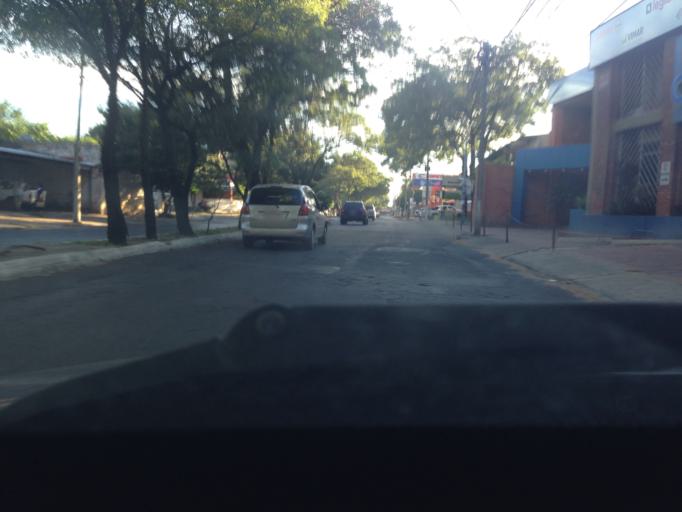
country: PY
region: Central
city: Lambare
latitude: -25.3152
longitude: -57.5895
